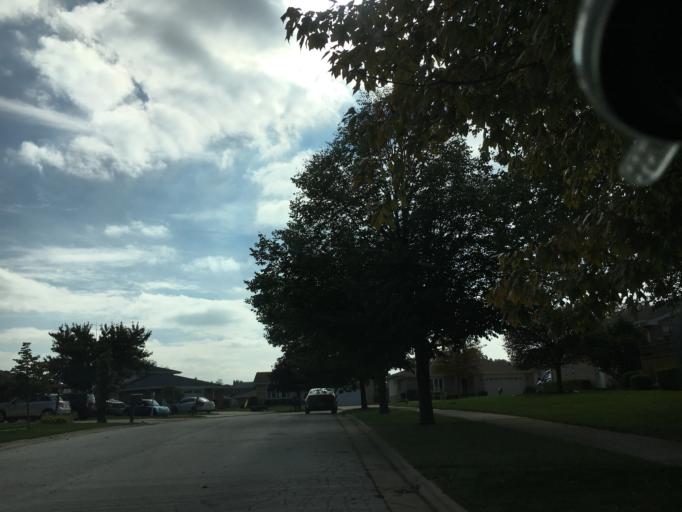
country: US
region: Illinois
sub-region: Cook County
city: Tinley Park
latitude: 41.6091
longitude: -87.7804
